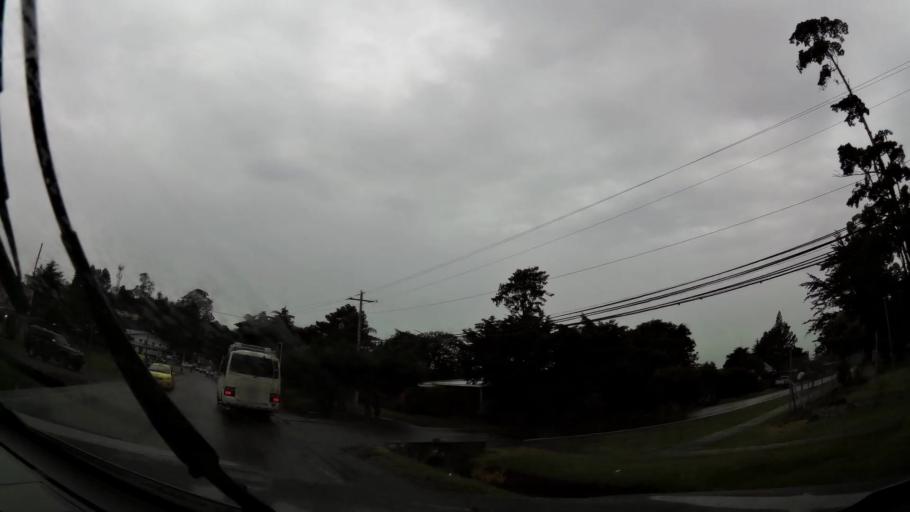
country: PA
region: Chiriqui
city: Volcan
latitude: 8.7801
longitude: -82.6419
